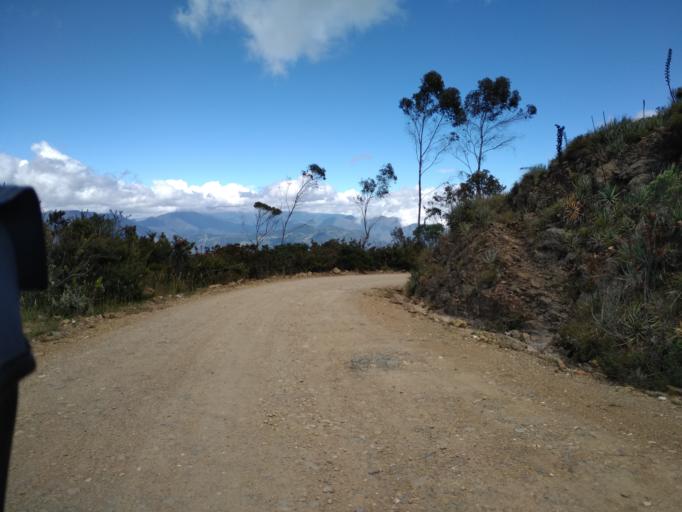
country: CO
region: Boyaca
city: Duitama
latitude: 5.9370
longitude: -73.1029
